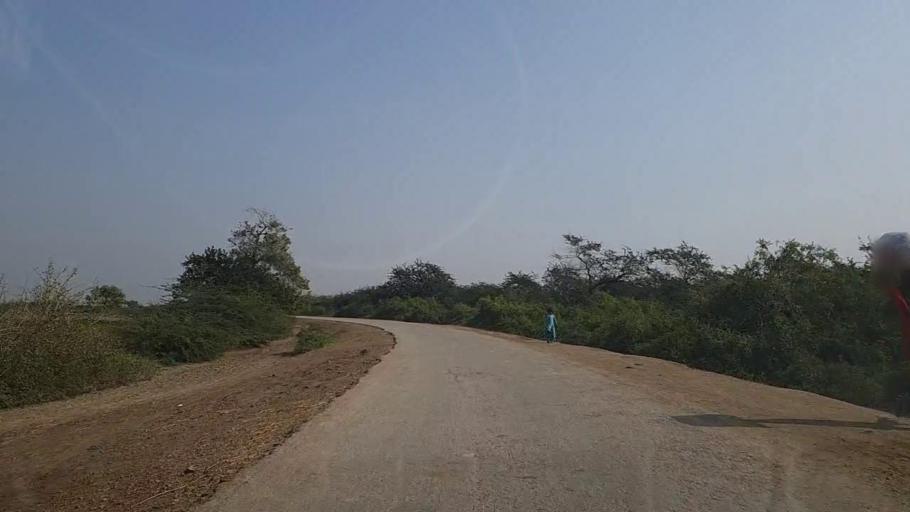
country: PK
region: Sindh
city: Keti Bandar
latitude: 24.2434
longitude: 67.7016
